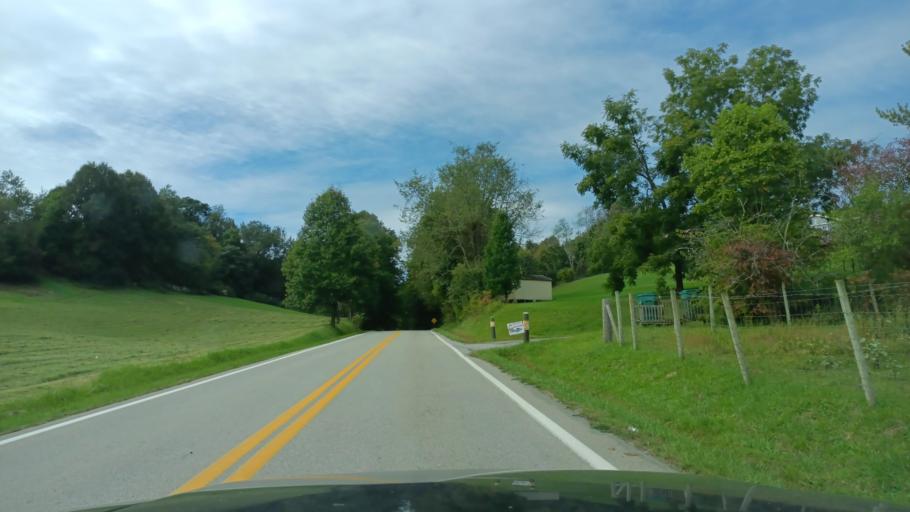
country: US
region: West Virginia
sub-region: Harrison County
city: Bridgeport
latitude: 39.3037
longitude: -80.1613
